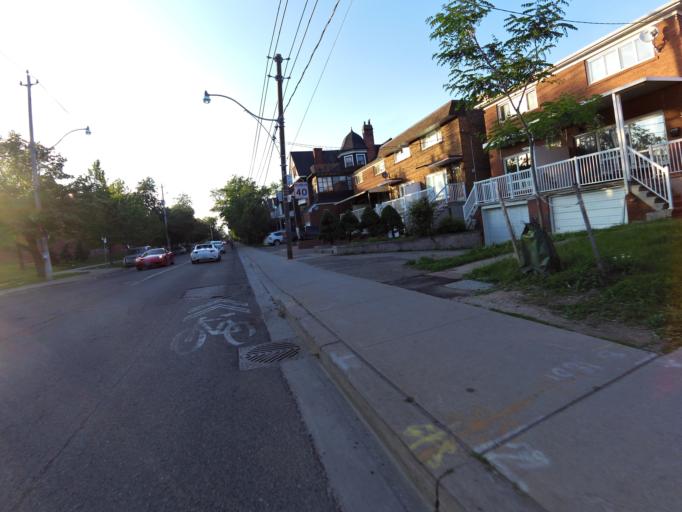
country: CA
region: Ontario
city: Toronto
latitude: 43.6513
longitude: -79.4401
